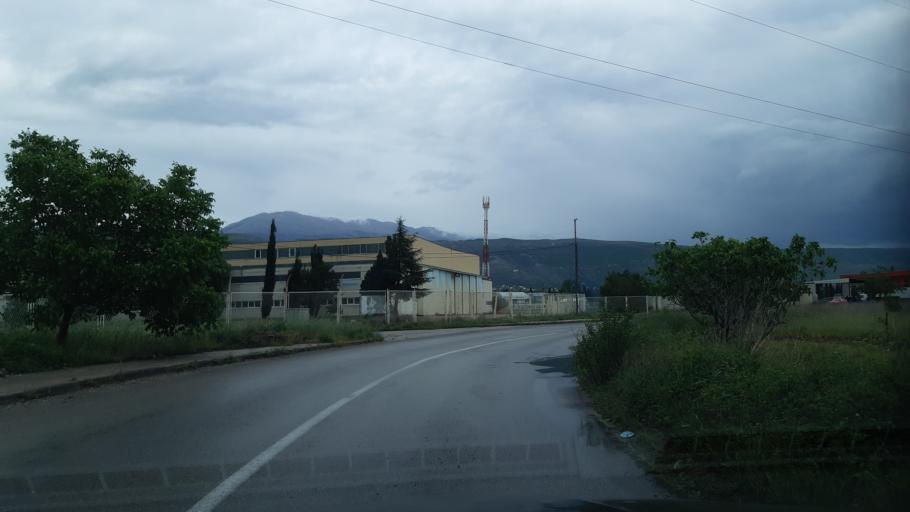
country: BA
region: Federation of Bosnia and Herzegovina
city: Rodoc
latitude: 43.3055
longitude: 17.8000
